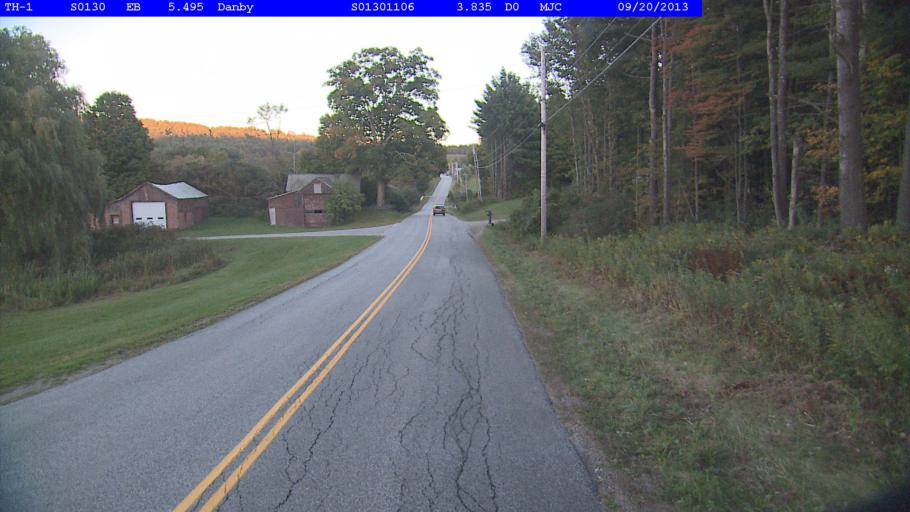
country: US
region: Vermont
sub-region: Bennington County
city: Manchester Center
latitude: 43.3561
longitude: -73.0548
